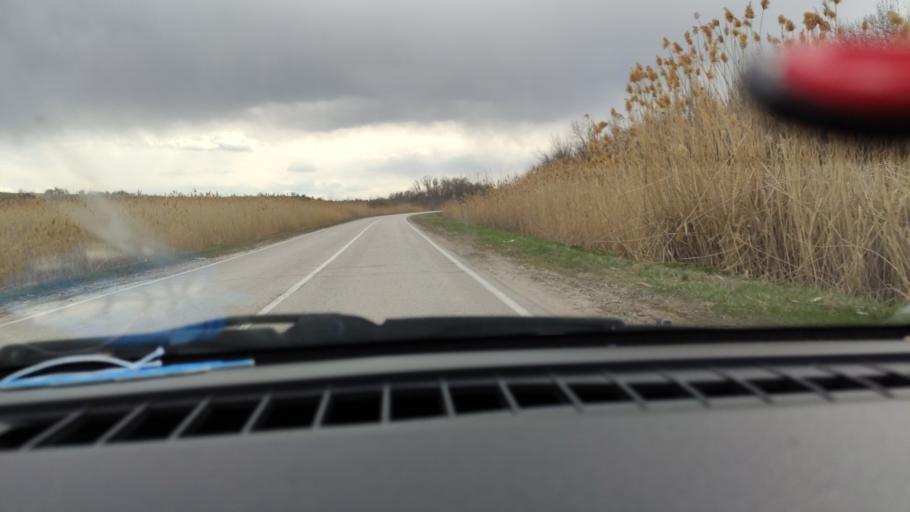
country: RU
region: Saratov
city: Privolzhskiy
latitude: 51.2572
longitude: 45.9431
